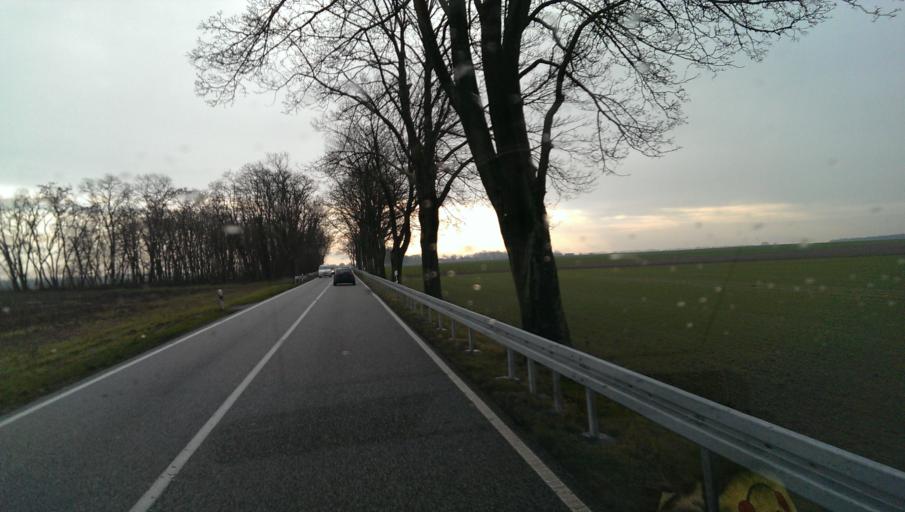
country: DE
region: Brandenburg
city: Juterbog
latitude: 51.9442
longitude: 13.1182
